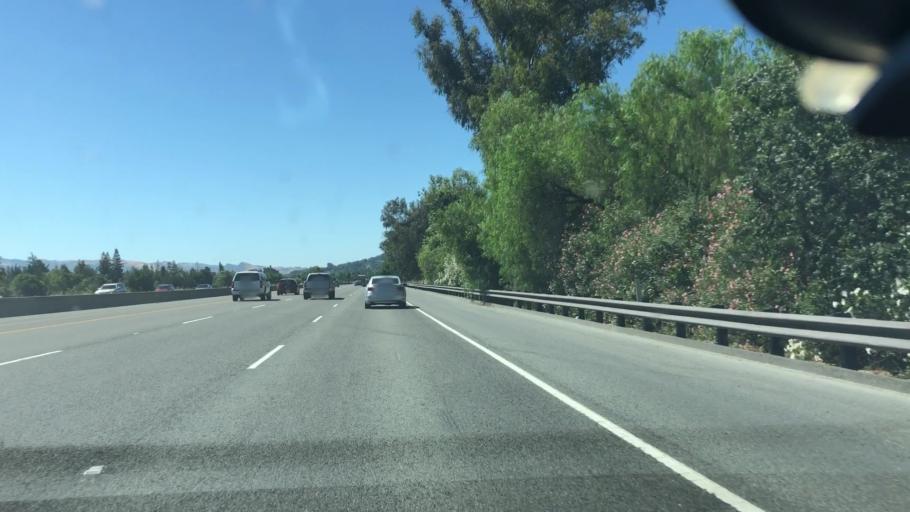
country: US
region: California
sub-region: Alameda County
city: Pleasanton
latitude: 37.6711
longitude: -121.9112
